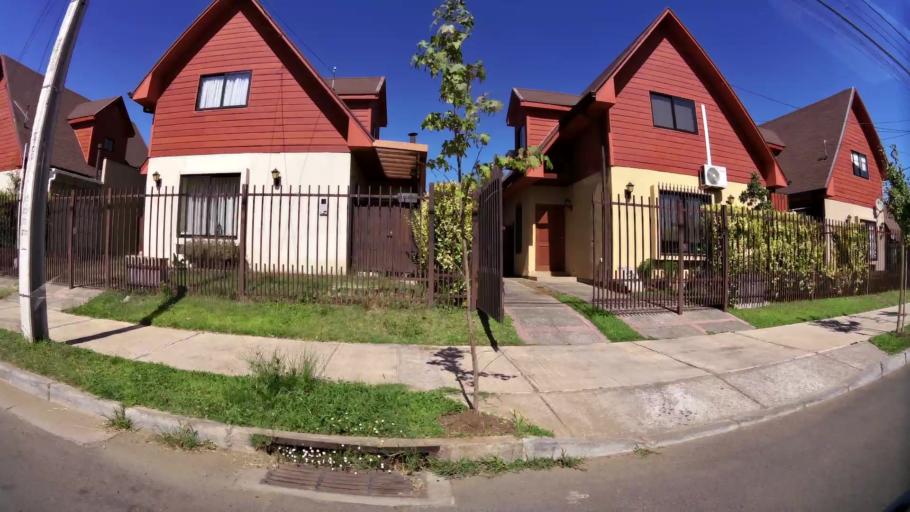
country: CL
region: Maule
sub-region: Provincia de Talca
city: Talca
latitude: -35.4281
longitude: -71.6163
